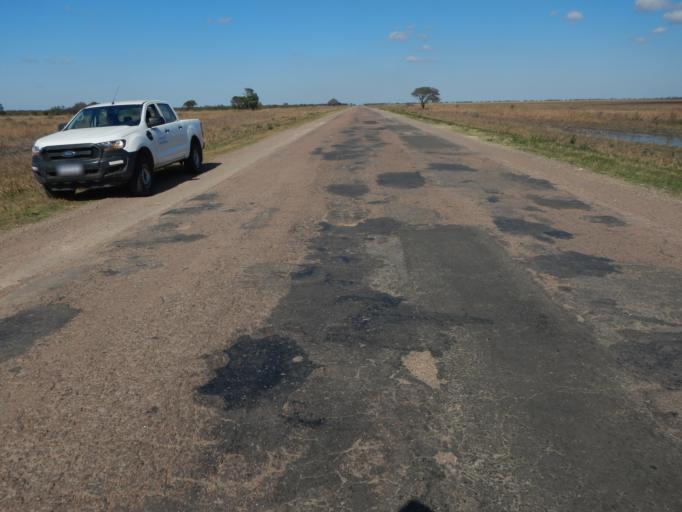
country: AR
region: Santa Fe
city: Tostado
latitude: -28.6979
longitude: -61.5357
